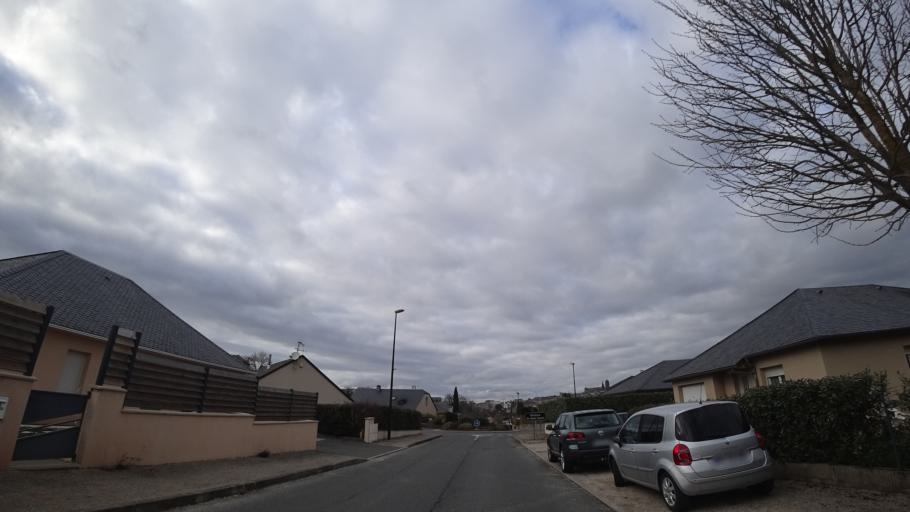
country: FR
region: Midi-Pyrenees
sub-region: Departement de l'Aveyron
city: Le Monastere
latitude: 44.3356
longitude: 2.5748
